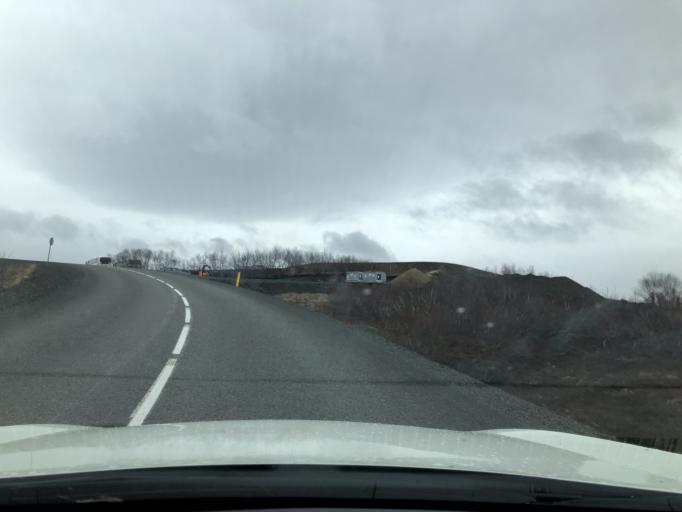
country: IS
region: Northeast
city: Laugar
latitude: 65.5921
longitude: -16.9153
